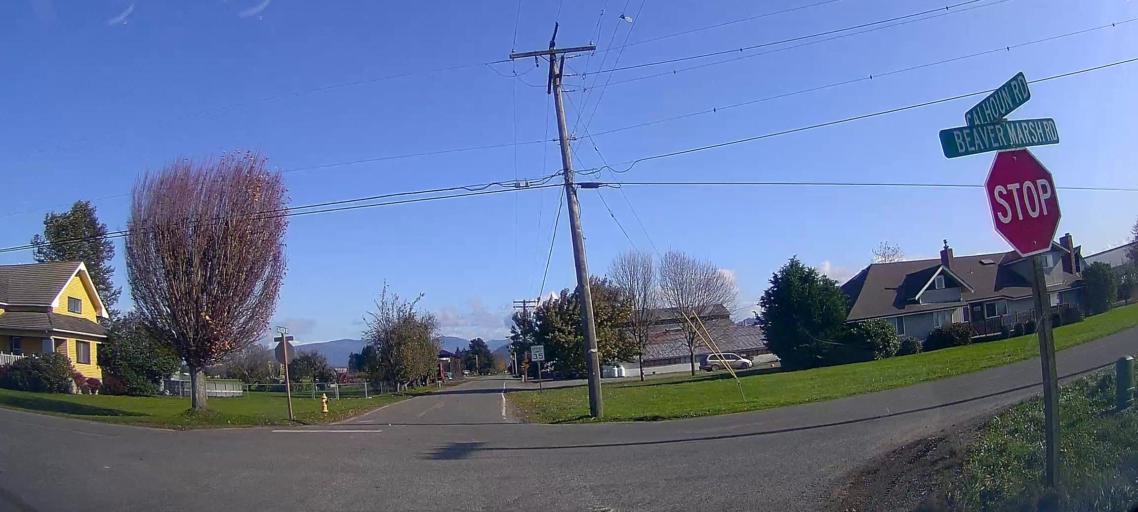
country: US
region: Washington
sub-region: Skagit County
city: Mount Vernon
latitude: 48.3993
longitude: -122.4008
